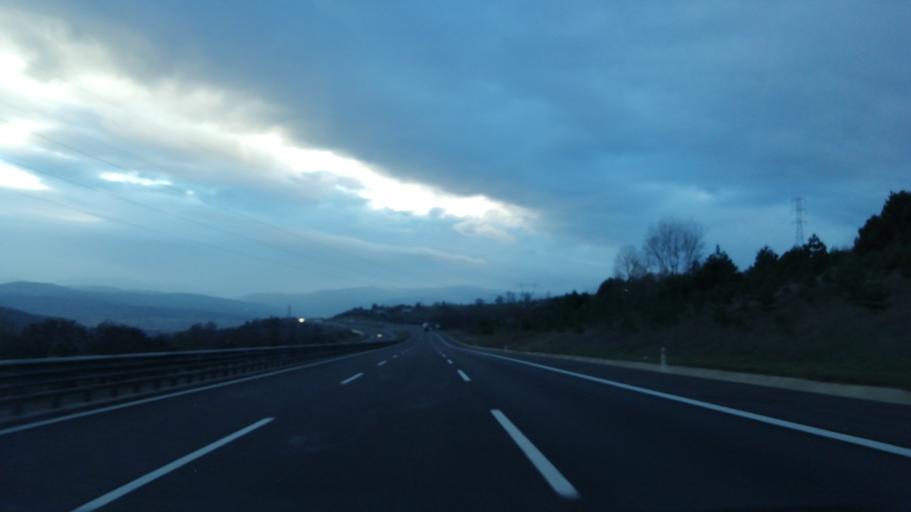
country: TR
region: Bolu
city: Bolu
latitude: 40.7311
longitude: 31.5174
